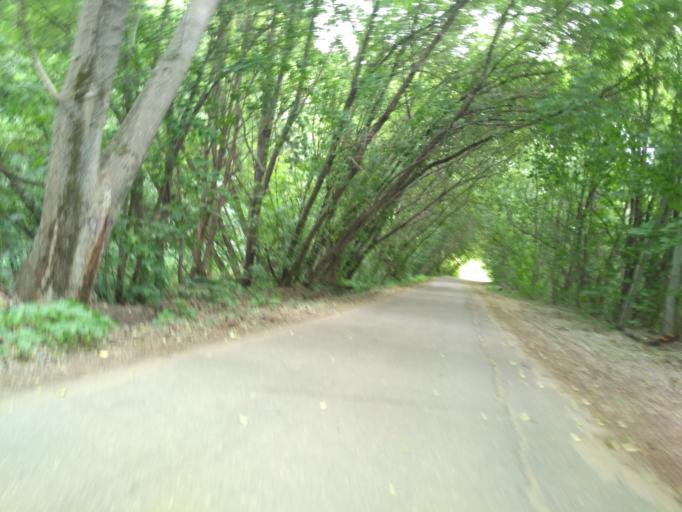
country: RU
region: Nizjnij Novgorod
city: Nizhniy Novgorod
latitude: 56.2943
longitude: 43.9680
